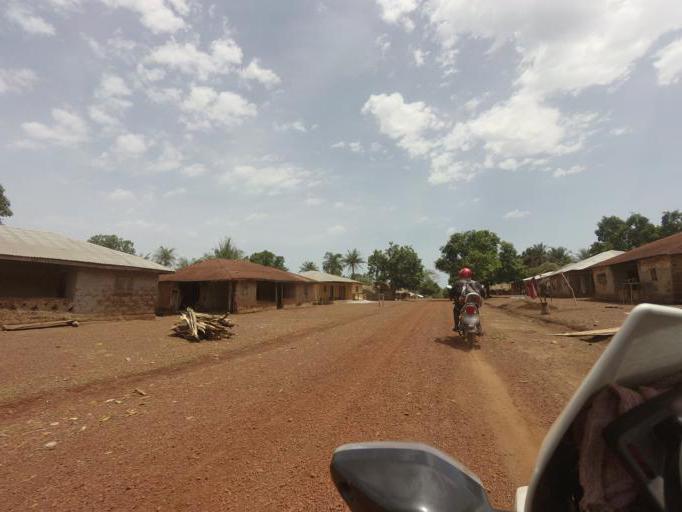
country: SL
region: Northern Province
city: Kamakwie
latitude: 9.5117
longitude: -12.2685
